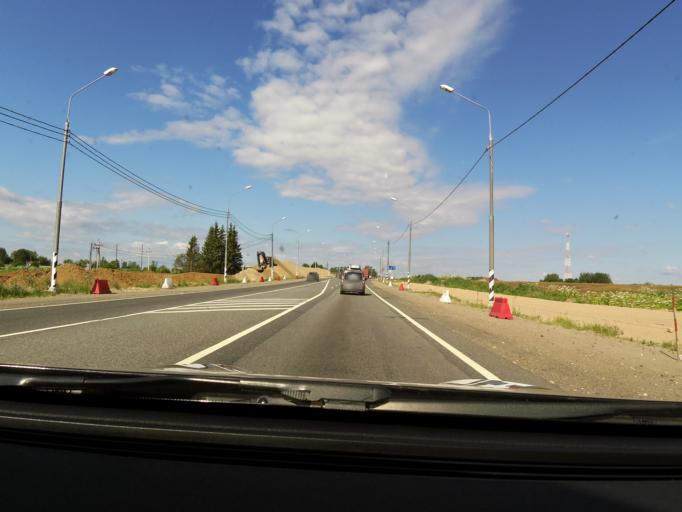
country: RU
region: Tverskaya
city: Tver
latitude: 56.7825
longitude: 35.9543
